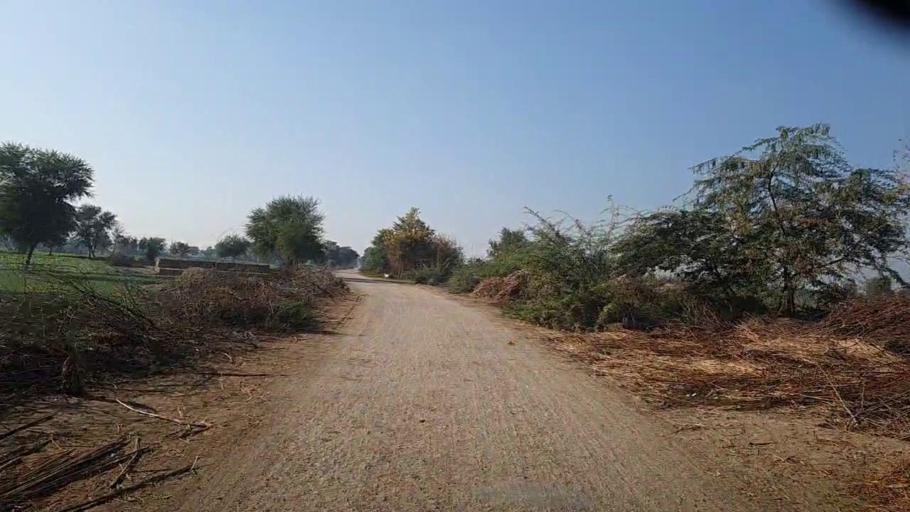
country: PK
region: Sindh
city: Darya Khan Marri
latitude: 26.6810
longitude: 68.3670
